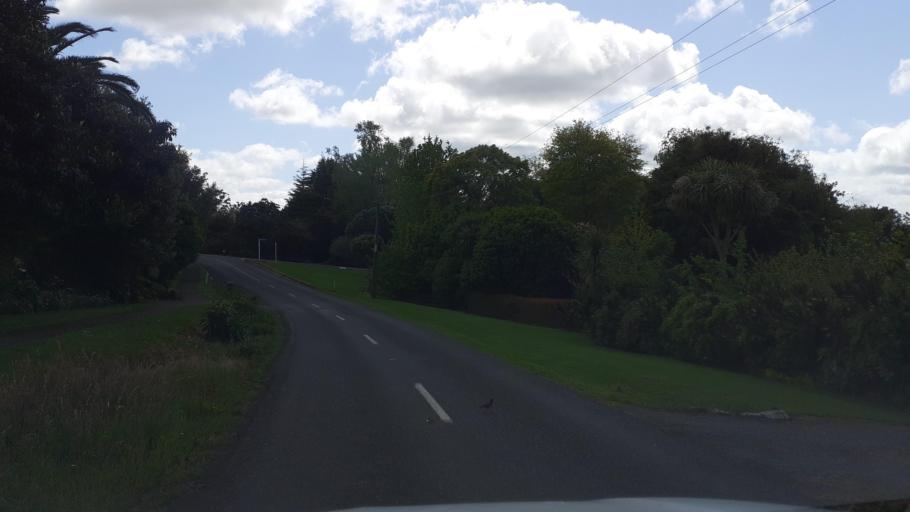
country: NZ
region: Northland
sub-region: Far North District
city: Kerikeri
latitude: -35.2400
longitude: 173.9590
